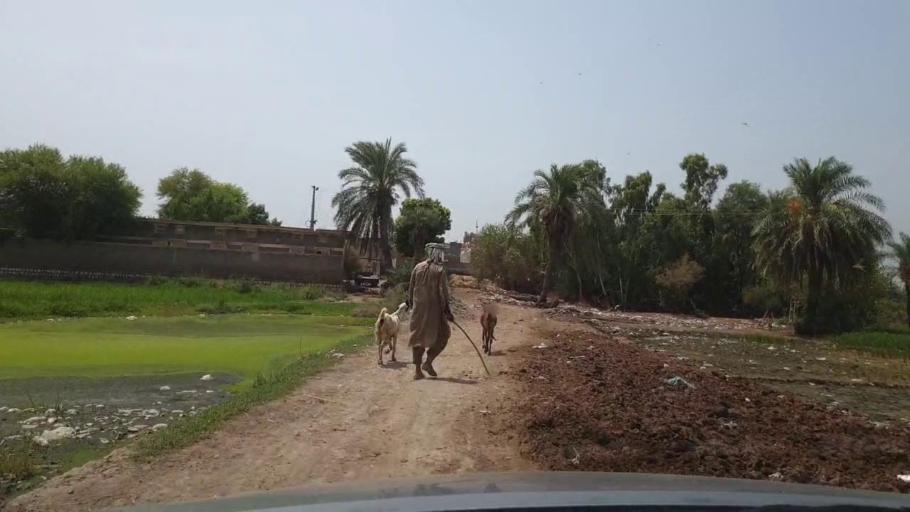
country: PK
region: Sindh
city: Madeji
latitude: 27.7872
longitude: 68.4339
